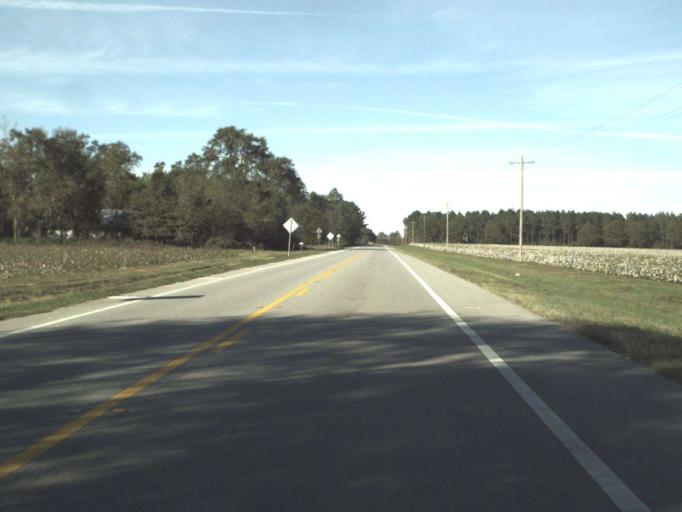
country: US
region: Alabama
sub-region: Escambia County
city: Atmore
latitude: 30.9117
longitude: -87.4792
